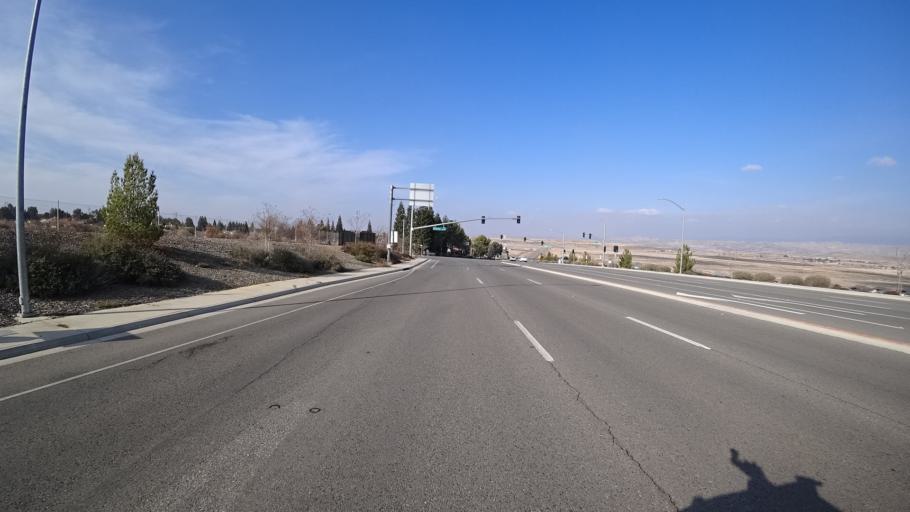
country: US
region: California
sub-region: Kern County
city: Oildale
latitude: 35.3989
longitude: -118.9139
